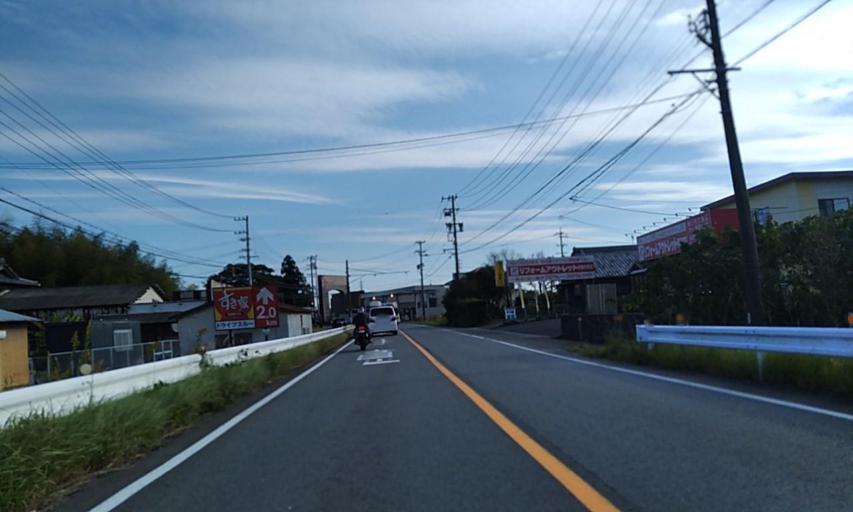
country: JP
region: Mie
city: Toba
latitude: 34.3470
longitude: 136.8128
